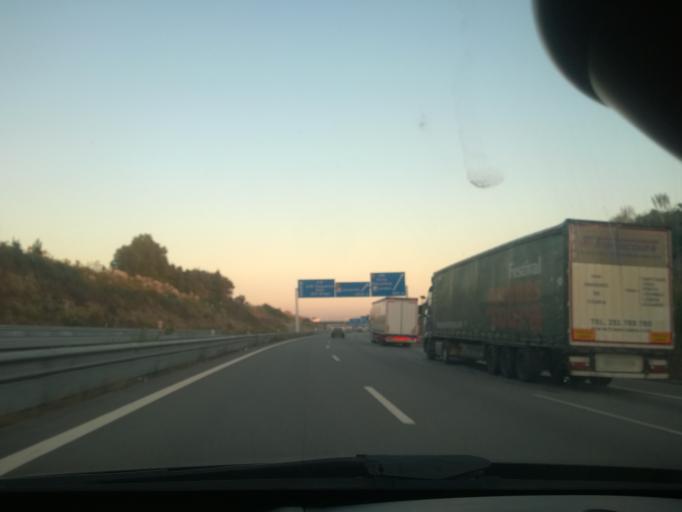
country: PT
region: Porto
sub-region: Matosinhos
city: Santa Cruz do Bispo
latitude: 41.2312
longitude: -8.6816
